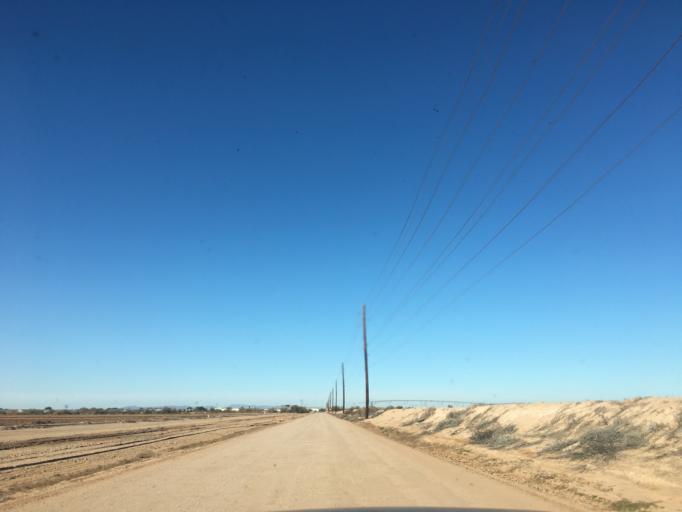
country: US
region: Arizona
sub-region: Pinal County
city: Maricopa
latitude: 33.0224
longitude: -112.0137
